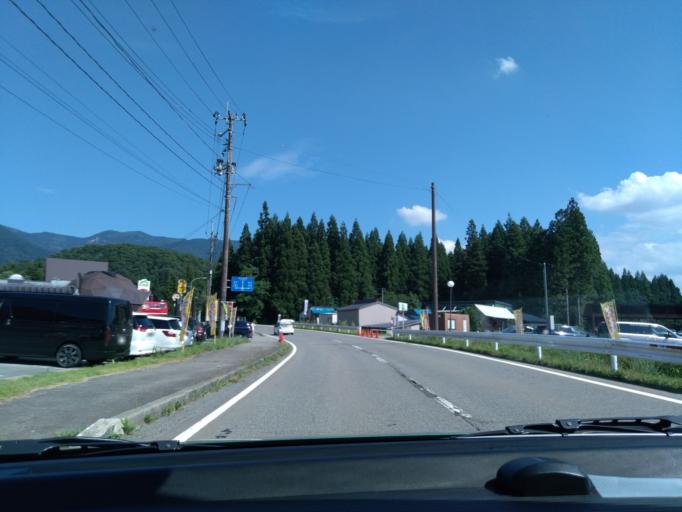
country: JP
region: Akita
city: Kakunodatemachi
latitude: 39.7400
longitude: 140.7139
